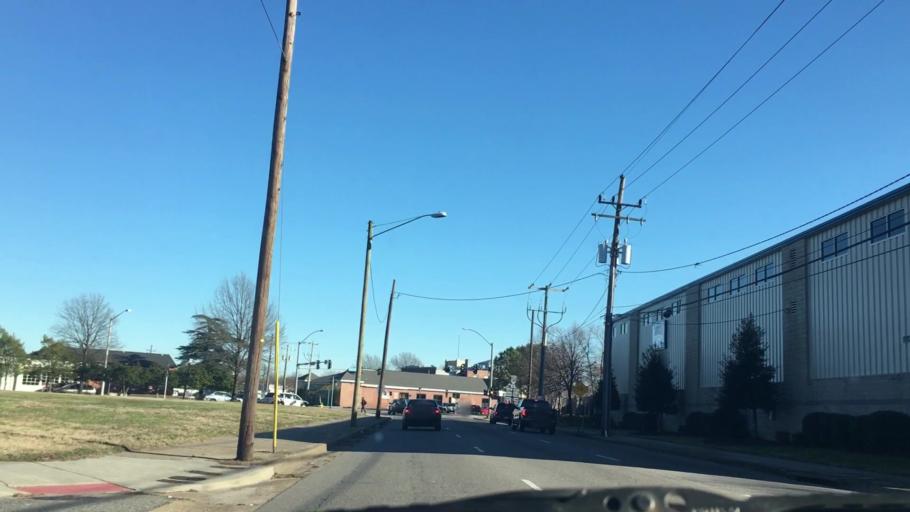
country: US
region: Virginia
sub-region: City of Norfolk
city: Norfolk
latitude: 36.8704
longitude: -76.2813
